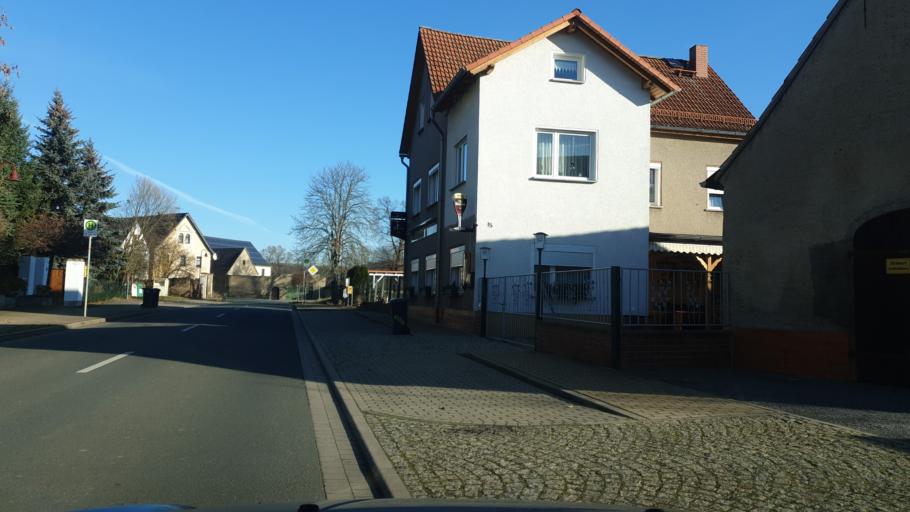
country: DE
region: Thuringia
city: Hartmannsdorf
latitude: 50.9845
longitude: 11.9872
